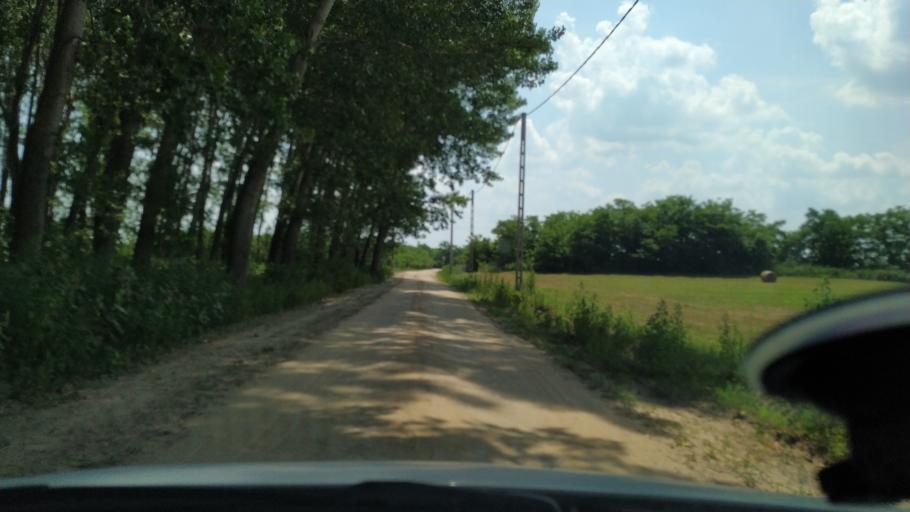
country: HU
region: Pest
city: Szentmartonkata
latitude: 47.4254
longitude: 19.7132
